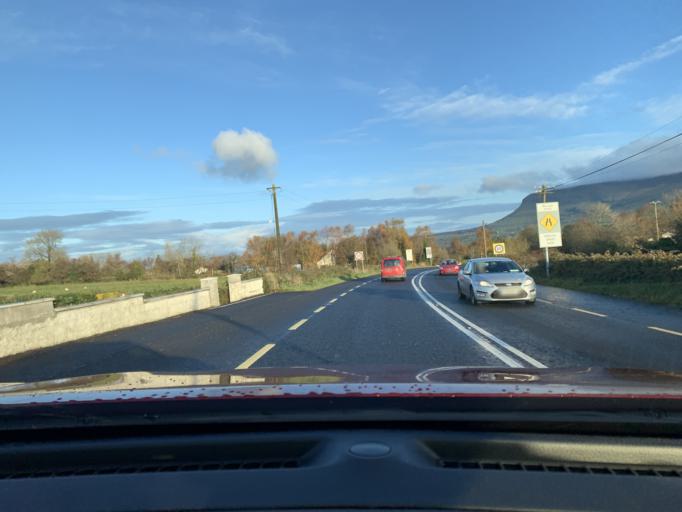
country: IE
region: Connaught
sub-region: Sligo
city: Sligo
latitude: 54.3116
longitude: -8.4844
